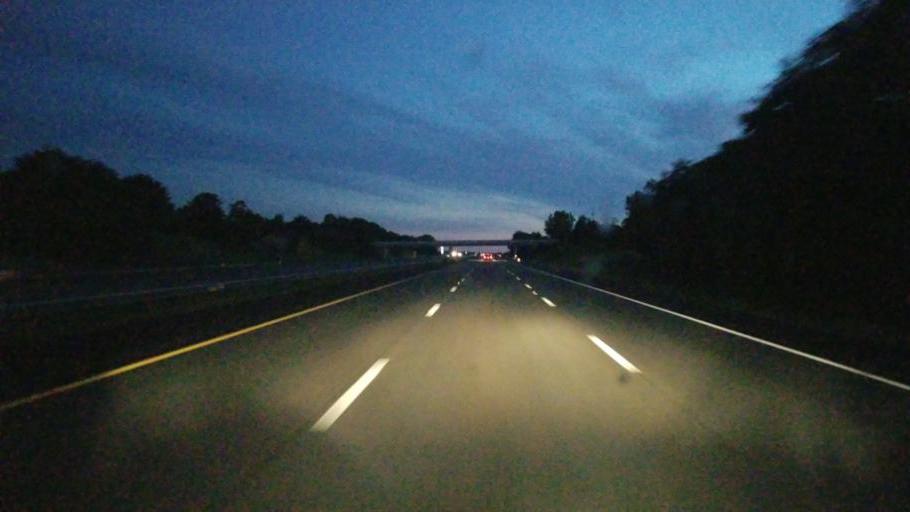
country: US
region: Ohio
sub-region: Medina County
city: Westfield Center
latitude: 41.0044
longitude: -81.9586
